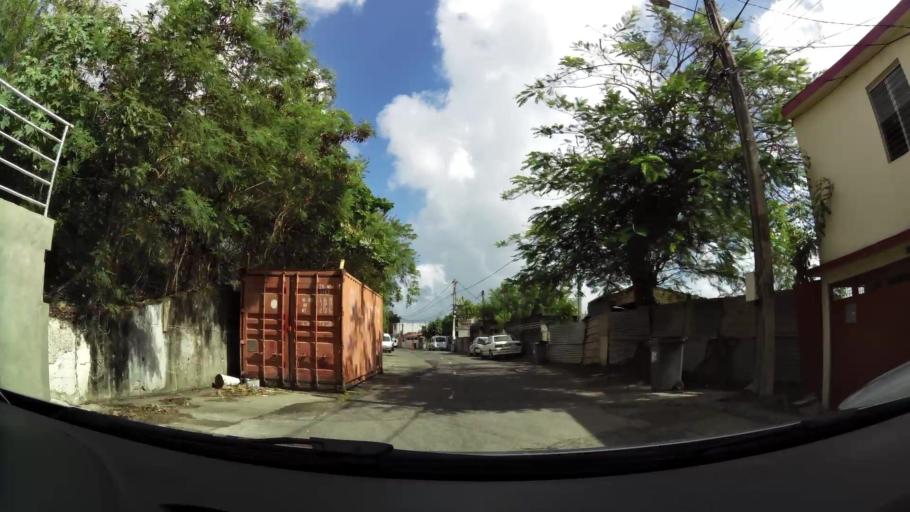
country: MQ
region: Martinique
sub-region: Martinique
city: Fort-de-France
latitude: 14.6001
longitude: -61.0883
